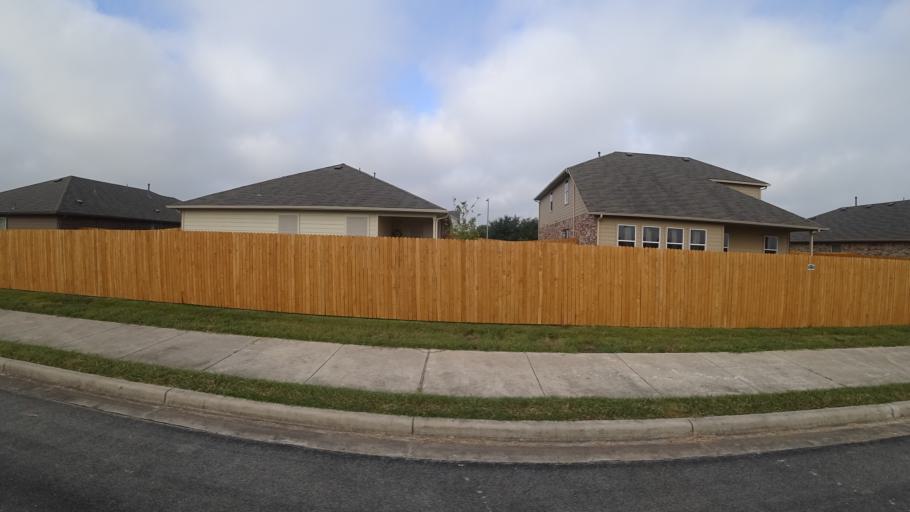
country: US
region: Texas
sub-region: Travis County
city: Pflugerville
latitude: 30.3630
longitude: -97.6418
